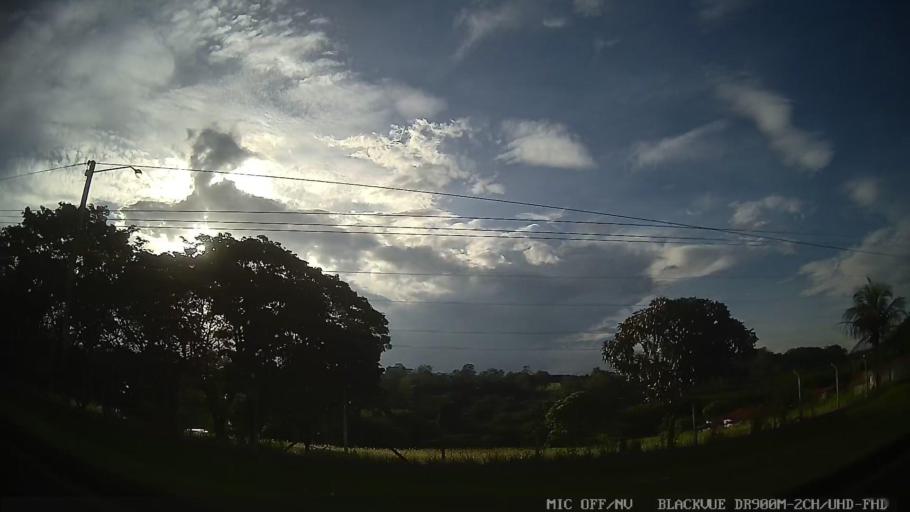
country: BR
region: Sao Paulo
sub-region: Tiete
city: Tiete
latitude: -23.0950
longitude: -47.7231
